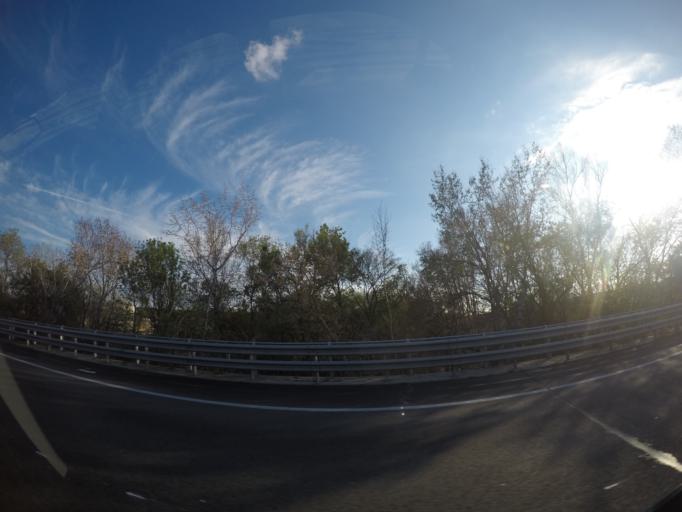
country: ES
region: Catalonia
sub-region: Provincia de Barcelona
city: Vilafranca del Penedes
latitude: 41.3307
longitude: 1.6694
